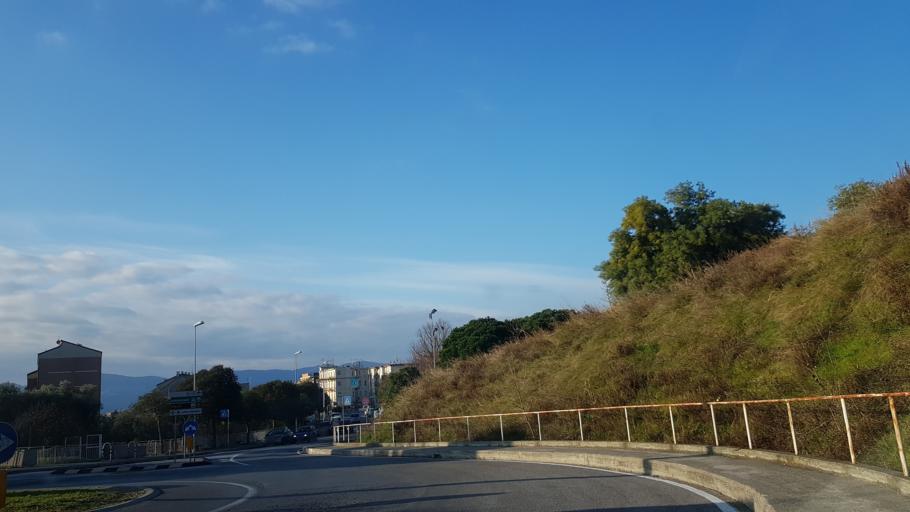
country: IT
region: Liguria
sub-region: Provincia di Savona
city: Savona
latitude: 44.3054
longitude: 8.4617
